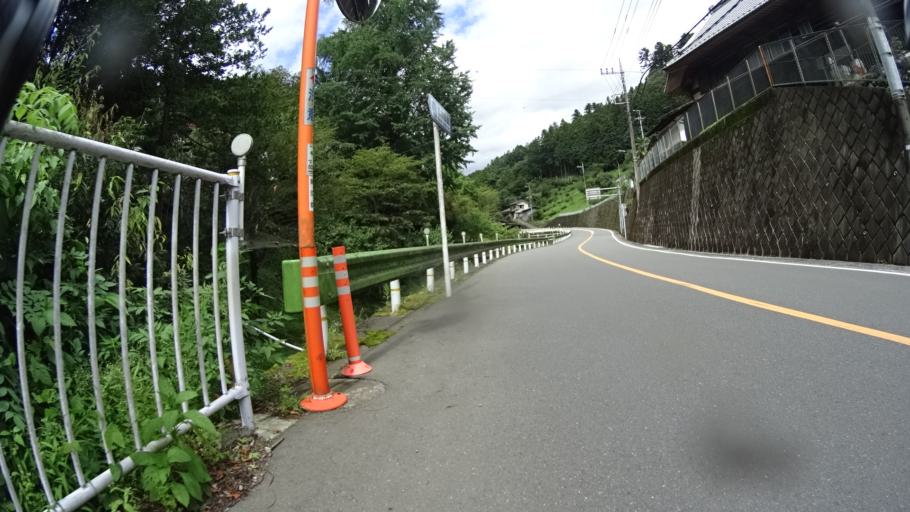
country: JP
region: Tokyo
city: Ome
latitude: 35.8357
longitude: 139.2079
